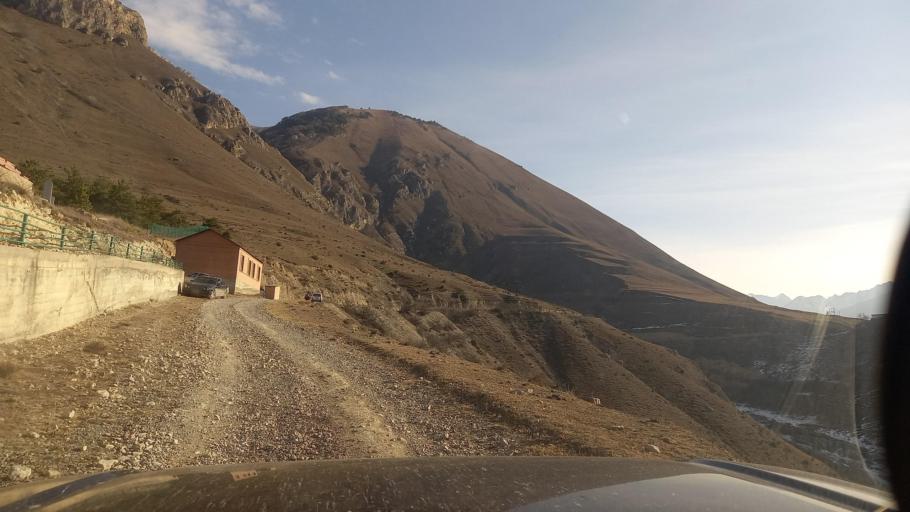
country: RU
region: Ingushetiya
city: Dzhayrakh
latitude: 42.8466
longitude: 44.6557
